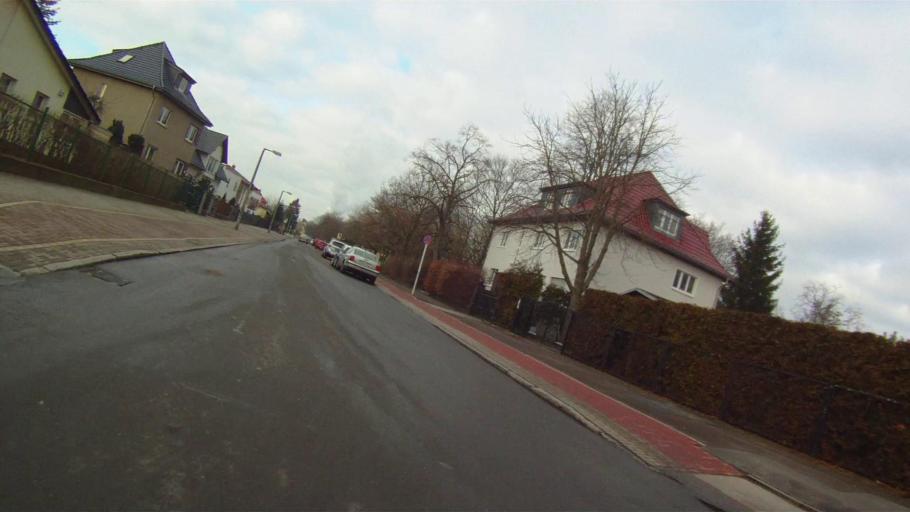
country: DE
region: Berlin
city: Karlshorst
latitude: 52.4930
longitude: 13.5395
